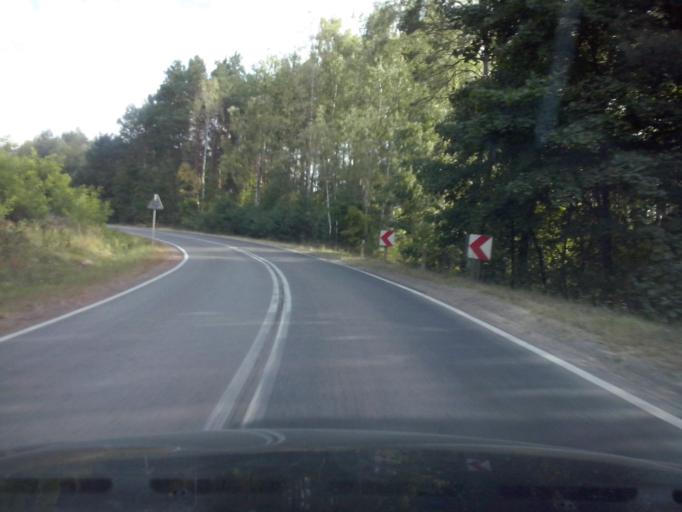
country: PL
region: Swietokrzyskie
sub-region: Powiat kielecki
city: Rakow
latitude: 50.7021
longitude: 21.0553
